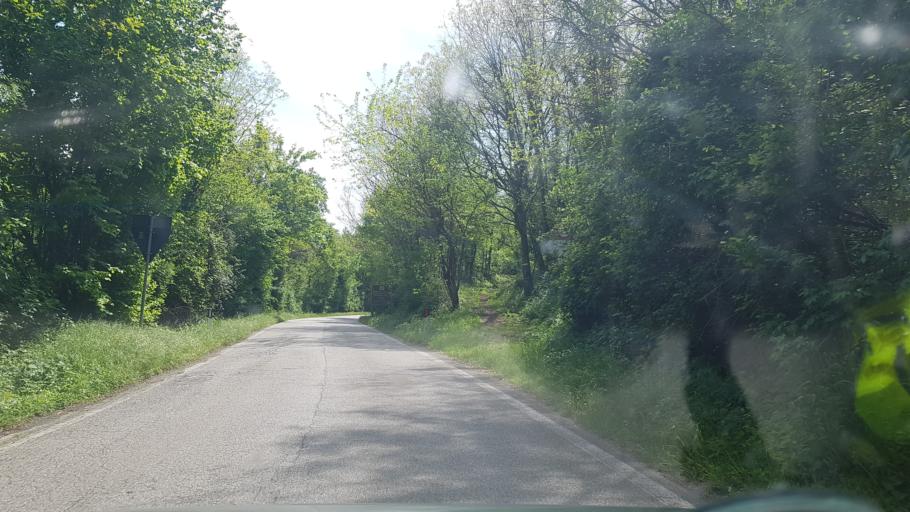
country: IT
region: Friuli Venezia Giulia
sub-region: Provincia di Gorizia
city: Savogna d'Isonzo
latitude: 45.8971
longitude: 13.5699
